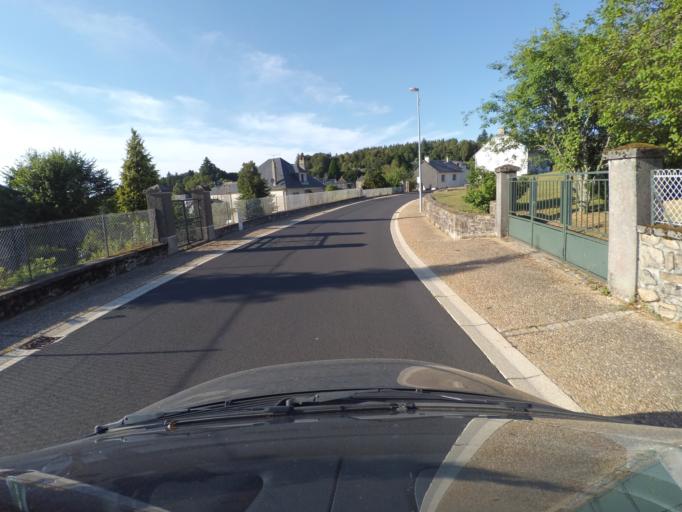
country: FR
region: Limousin
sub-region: Departement de la Correze
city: Bugeat
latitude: 45.7019
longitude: 2.0545
